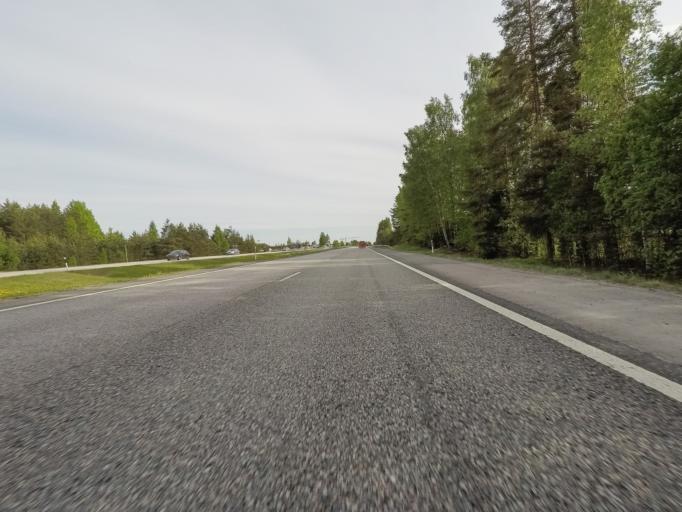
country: FI
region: Uusimaa
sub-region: Helsinki
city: Nurmijaervi
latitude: 60.5038
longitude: 24.8499
